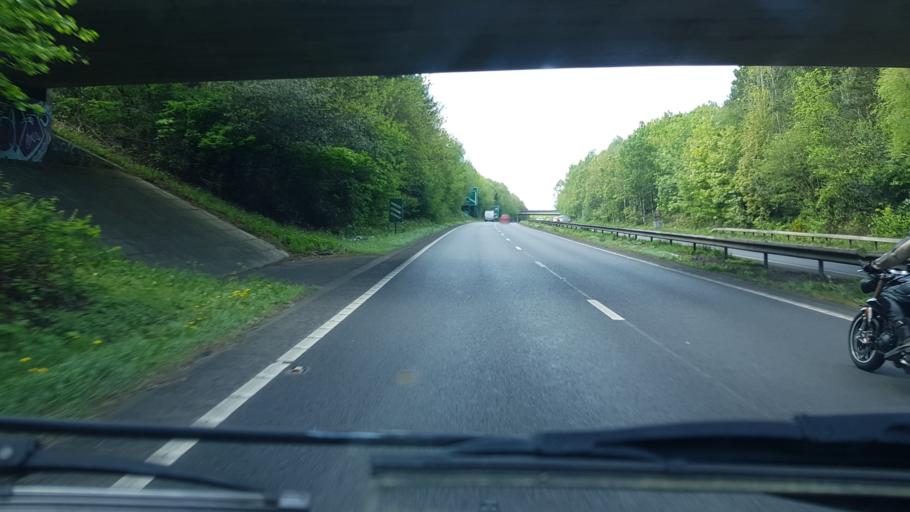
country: GB
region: England
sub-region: Kent
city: Pembury
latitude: 51.1415
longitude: 0.3128
